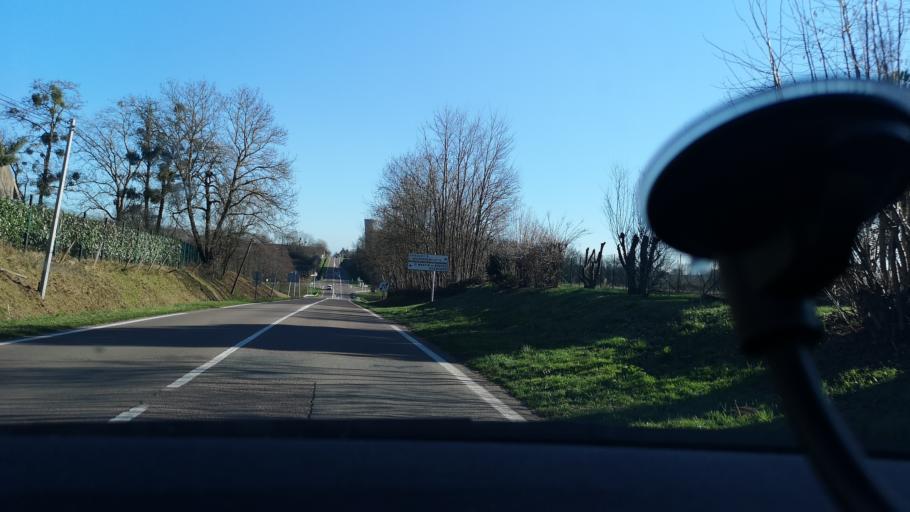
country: FR
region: Bourgogne
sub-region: Departement de Saone-et-Loire
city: Saint-Germain-du-Plain
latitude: 46.7572
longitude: 5.0046
